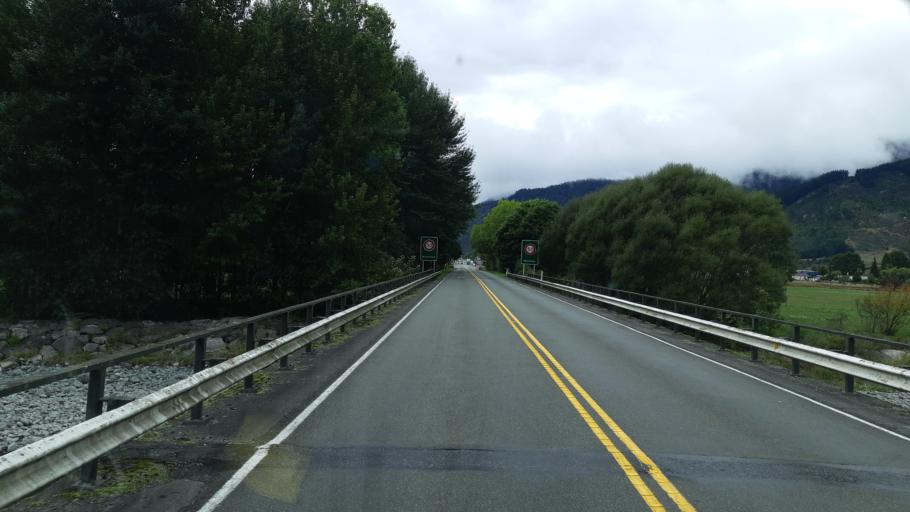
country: NZ
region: West Coast
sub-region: Buller District
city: Westport
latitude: -41.8000
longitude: 172.3184
